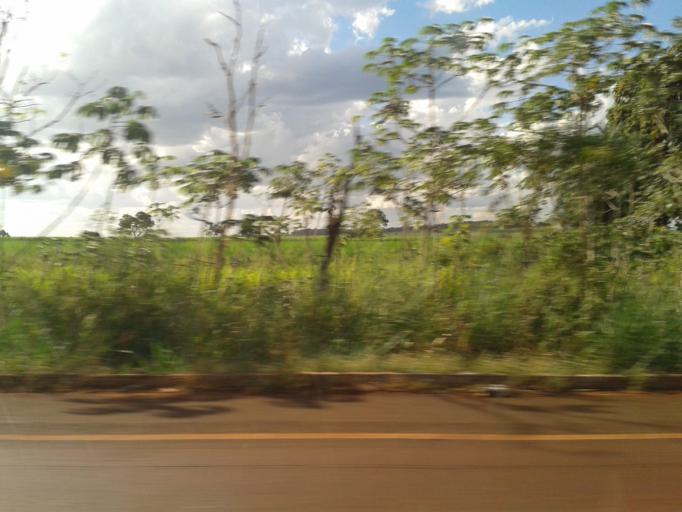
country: BR
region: Minas Gerais
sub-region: Santa Vitoria
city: Santa Vitoria
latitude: -18.6932
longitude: -49.9152
